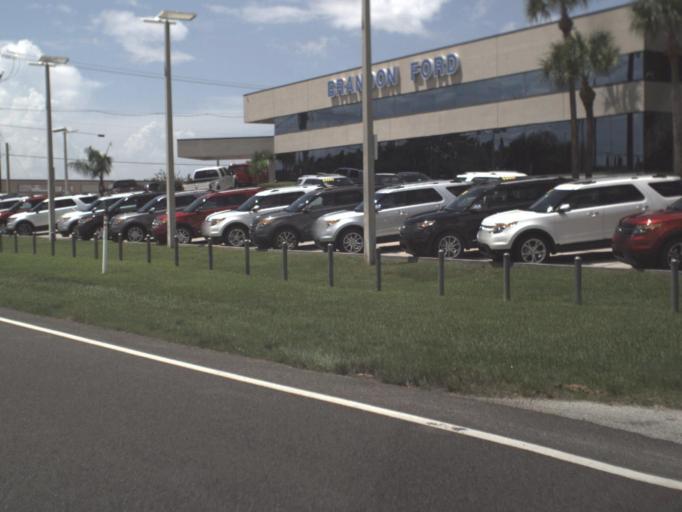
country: US
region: Florida
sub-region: Hillsborough County
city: Palm River-Clair Mel
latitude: 27.9504
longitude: -82.3544
